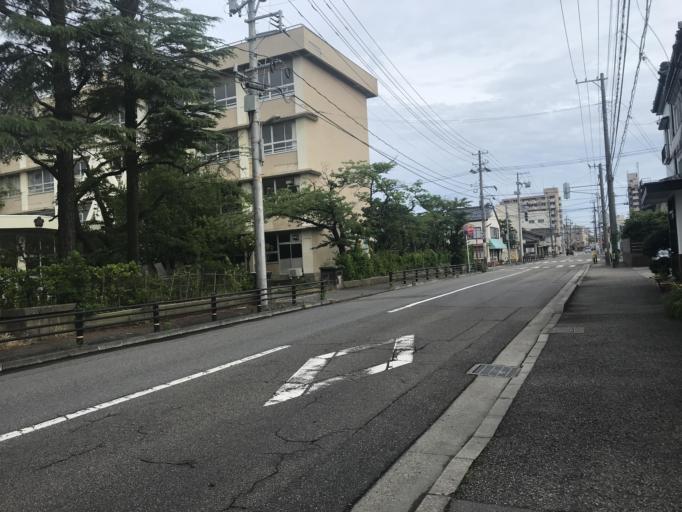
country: JP
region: Niigata
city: Niigata-shi
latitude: 37.9272
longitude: 139.0535
